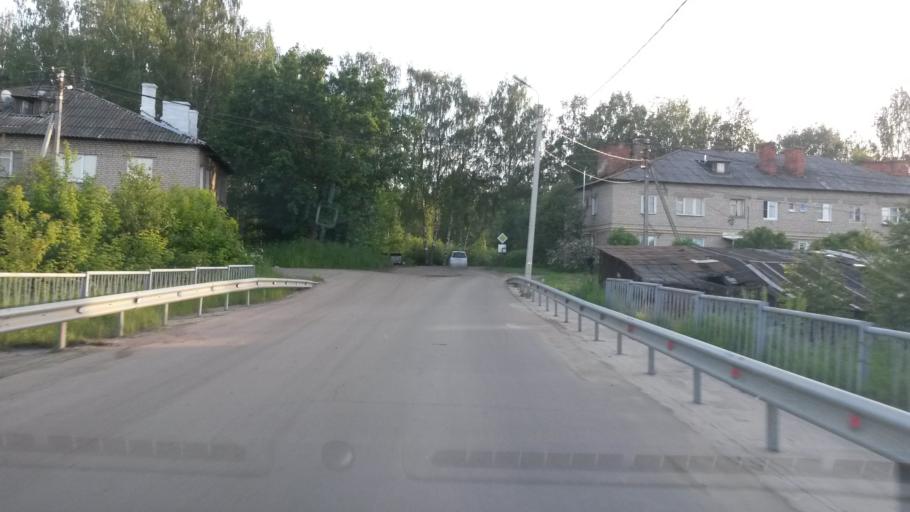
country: RU
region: Jaroslavl
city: Yaroslavl
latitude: 57.7012
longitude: 39.8245
